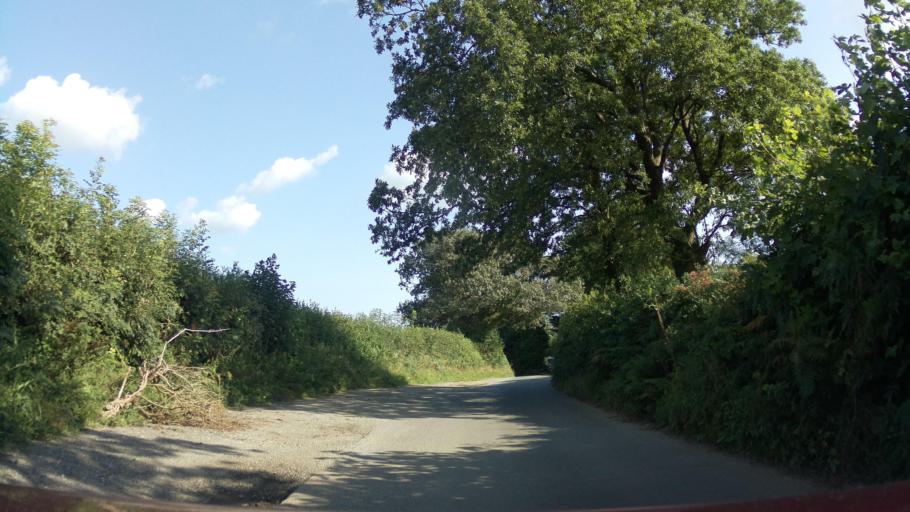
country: GB
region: England
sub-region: Devon
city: Buckfastleigh
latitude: 50.4447
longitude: -3.7927
